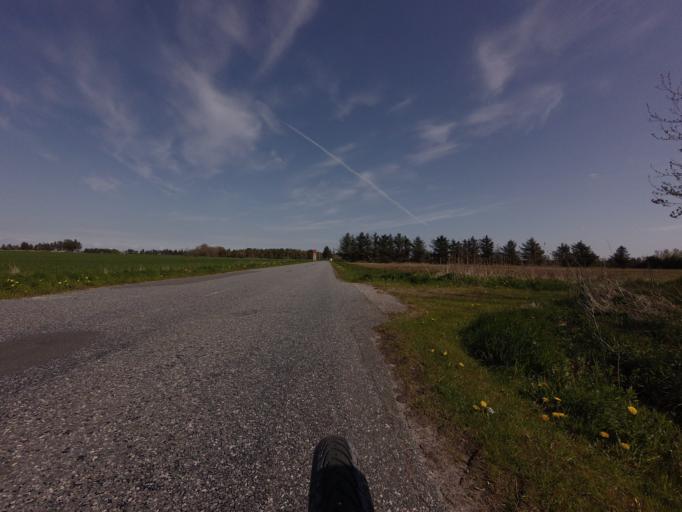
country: DK
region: North Denmark
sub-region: Jammerbugt Kommune
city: Pandrup
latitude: 57.2259
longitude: 9.6420
